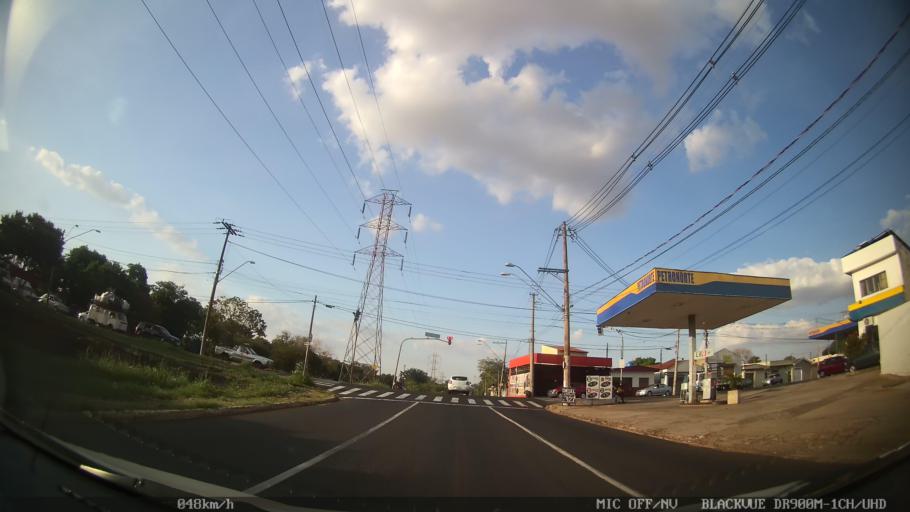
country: BR
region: Sao Paulo
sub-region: Ribeirao Preto
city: Ribeirao Preto
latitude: -21.1477
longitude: -47.8061
